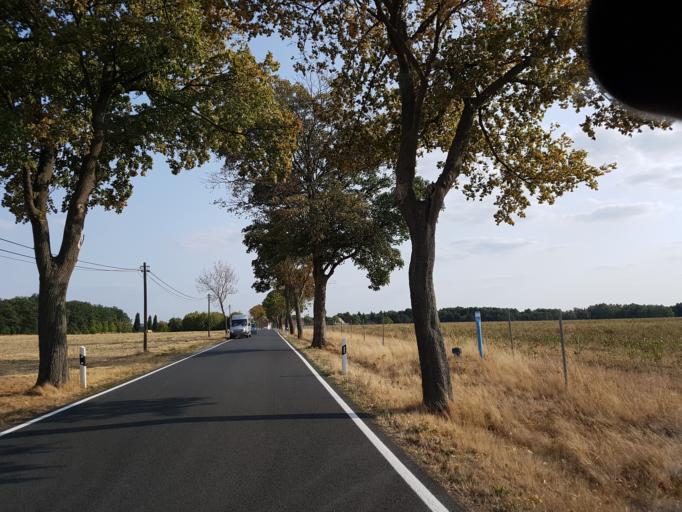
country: DE
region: Saxony-Anhalt
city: Pretzsch
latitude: 51.6913
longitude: 12.8246
